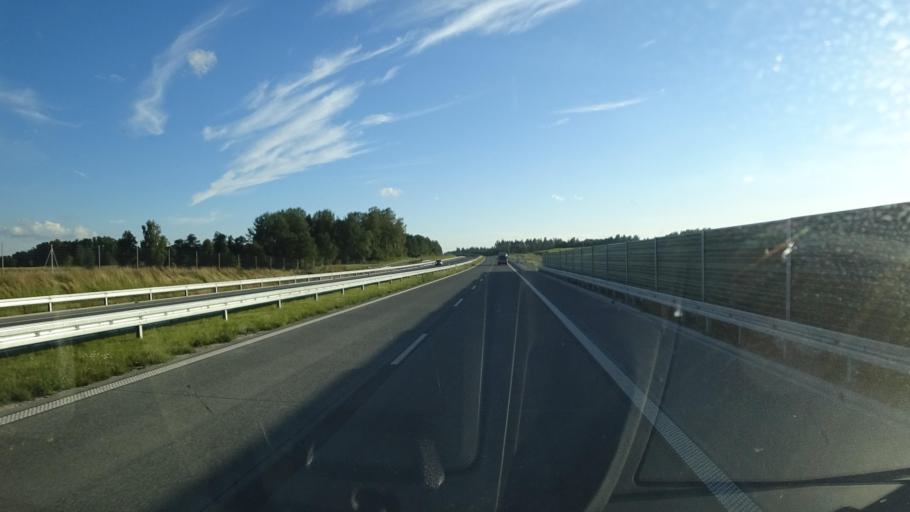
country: PL
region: Podlasie
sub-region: Powiat suwalski
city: Raczki
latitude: 53.9066
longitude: 22.7074
